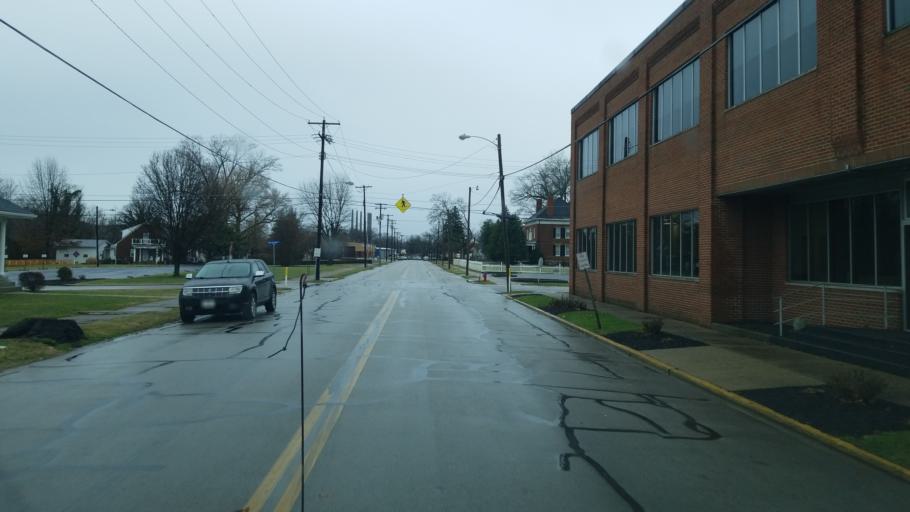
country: US
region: Kentucky
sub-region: Mason County
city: Maysville
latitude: 38.6426
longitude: -83.7381
